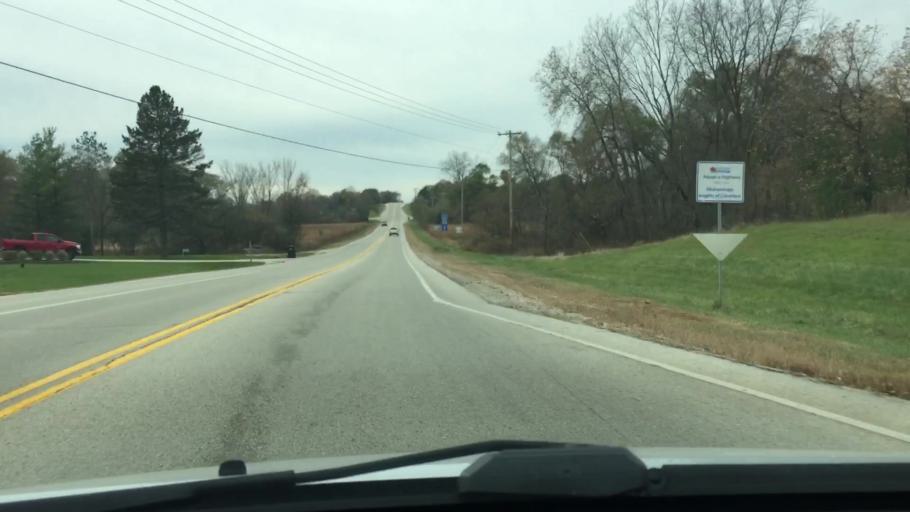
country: US
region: Wisconsin
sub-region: Waukesha County
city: Mukwonago
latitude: 42.8922
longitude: -88.2775
